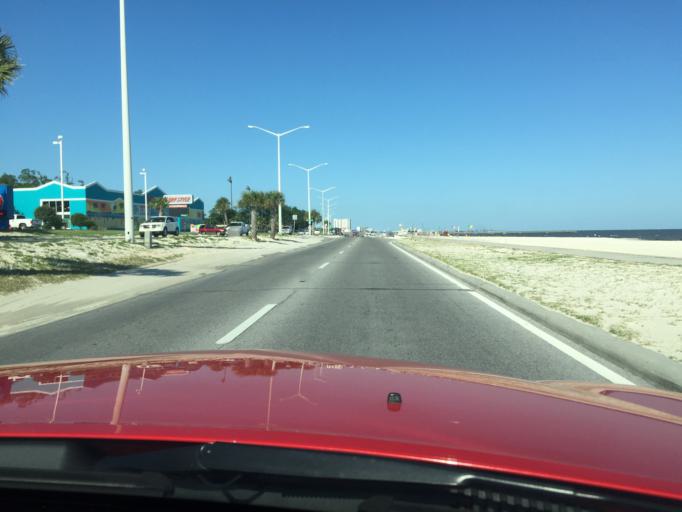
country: US
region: Mississippi
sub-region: Harrison County
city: Biloxi
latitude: 30.3899
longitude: -88.9824
